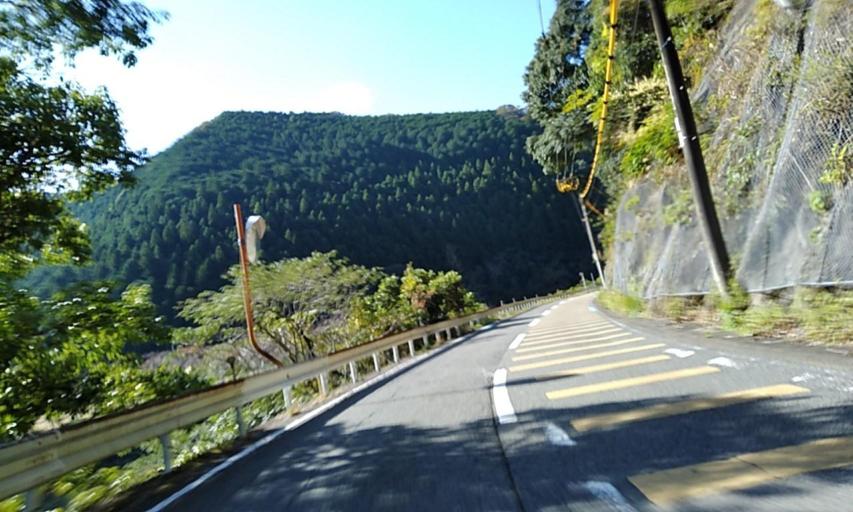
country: JP
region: Wakayama
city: Kainan
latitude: 34.0620
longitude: 135.3586
